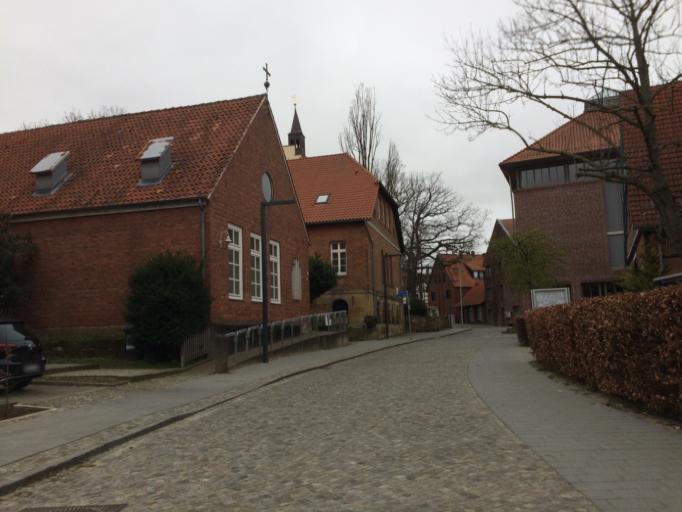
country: DE
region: Lower Saxony
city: Gehrden
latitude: 52.3135
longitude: 9.6023
